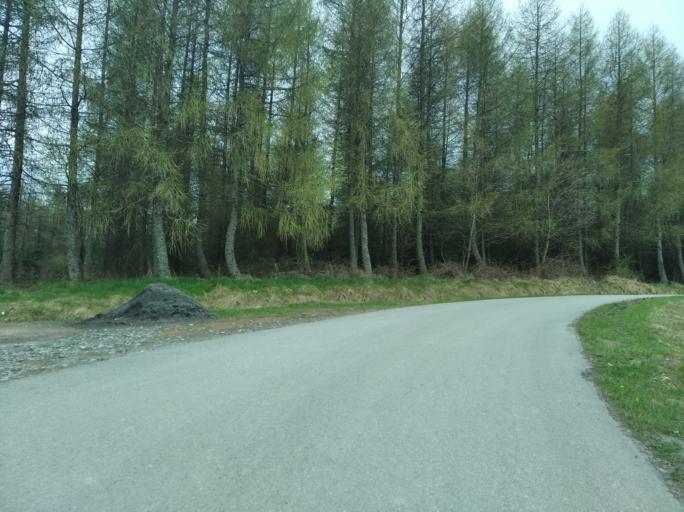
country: PL
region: Subcarpathian Voivodeship
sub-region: Powiat strzyzowski
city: Konieczkowa
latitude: 49.8222
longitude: 21.9115
